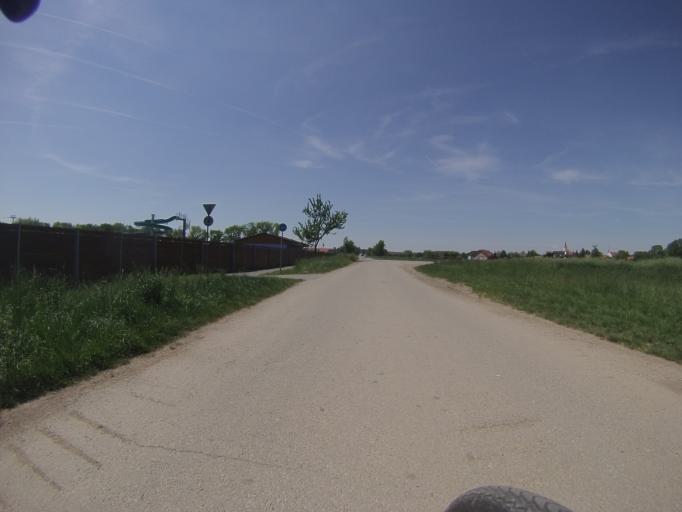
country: CZ
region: South Moravian
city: Zabcice
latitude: 49.0176
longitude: 16.6124
